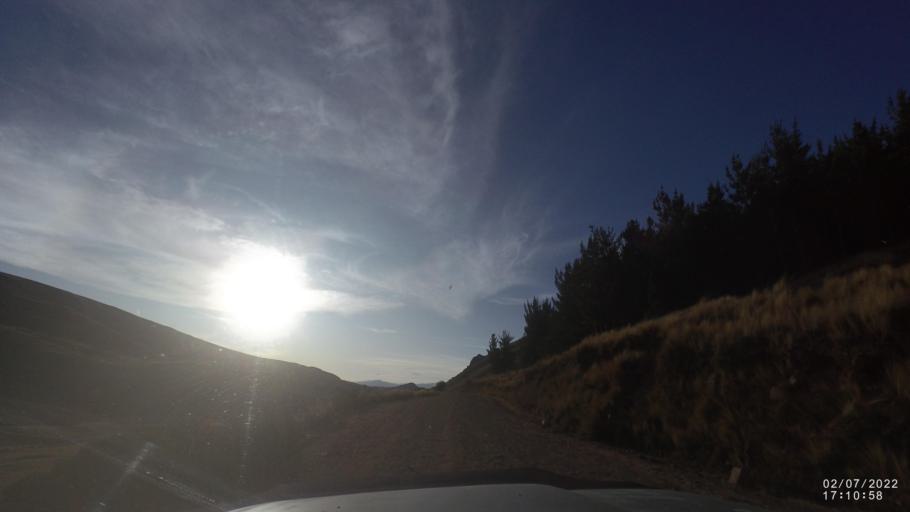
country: BO
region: Cochabamba
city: Irpa Irpa
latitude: -17.8935
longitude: -66.5625
